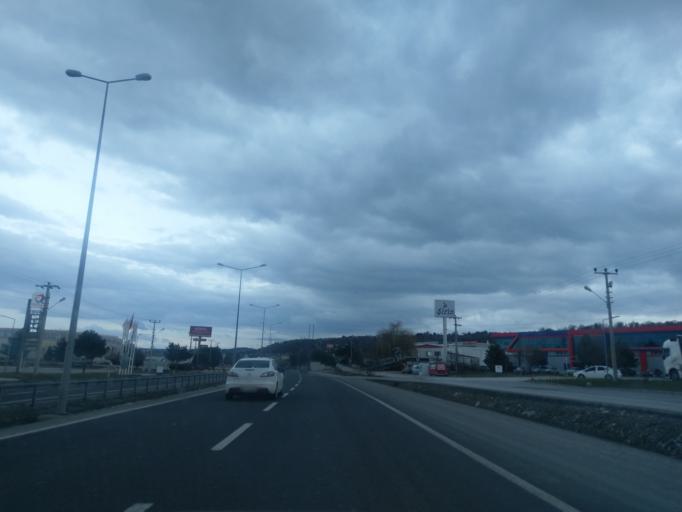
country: TR
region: Kuetahya
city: Kutahya
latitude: 39.3796
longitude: 30.0483
